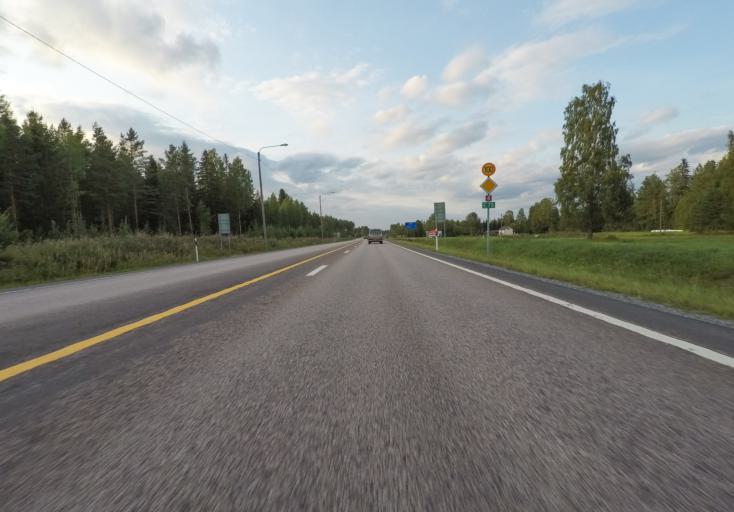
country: FI
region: Paijanne Tavastia
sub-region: Lahti
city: Hartola
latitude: 61.4862
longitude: 25.9801
